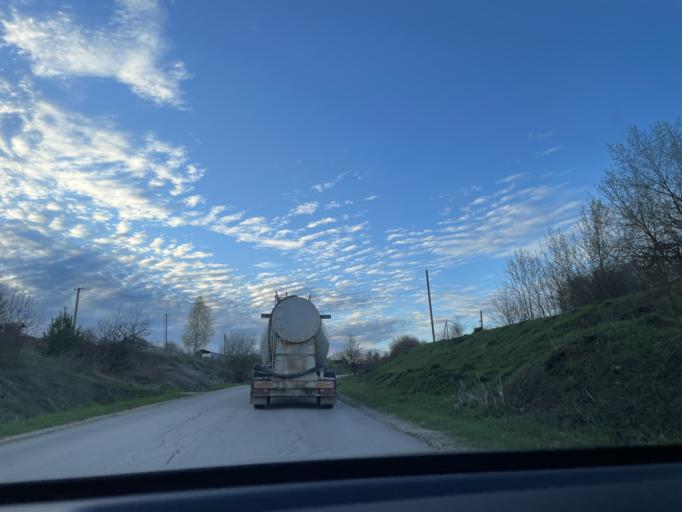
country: RU
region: Moskovskaya
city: Serpukhov
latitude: 54.8266
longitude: 37.4287
